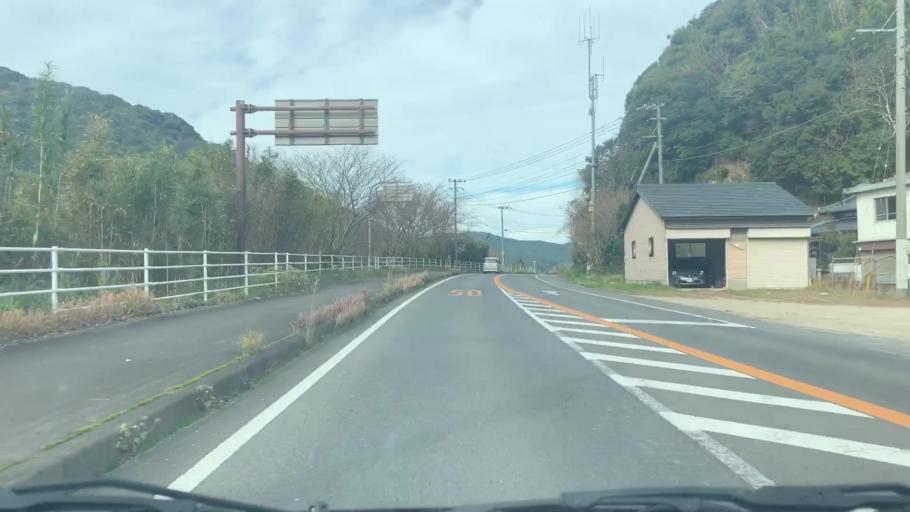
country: JP
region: Saga Prefecture
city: Karatsu
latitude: 33.3639
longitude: 130.0082
